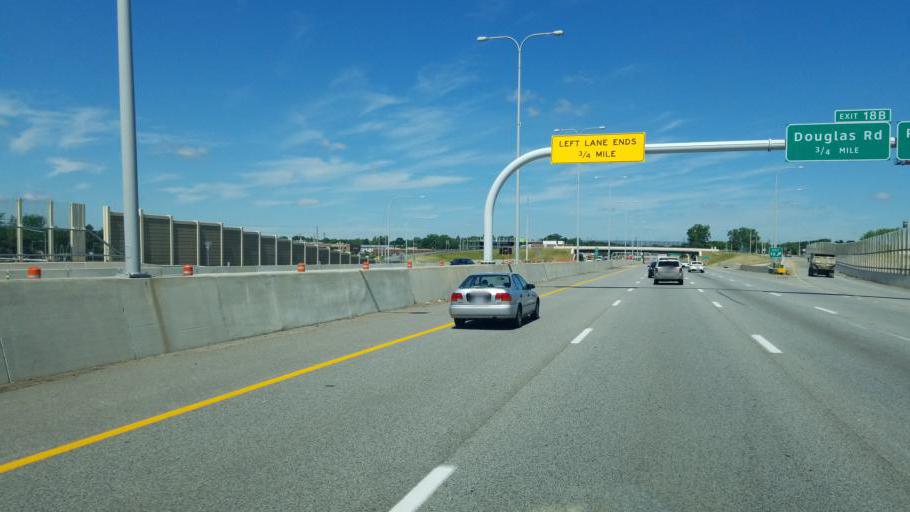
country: US
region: Ohio
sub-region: Lucas County
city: Toledo
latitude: 41.6784
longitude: -83.5880
